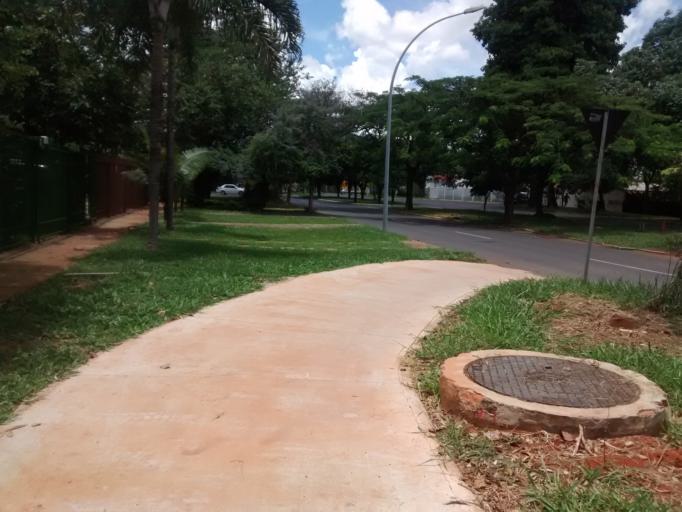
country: BR
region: Federal District
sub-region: Brasilia
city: Brasilia
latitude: -15.8112
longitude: -47.9089
